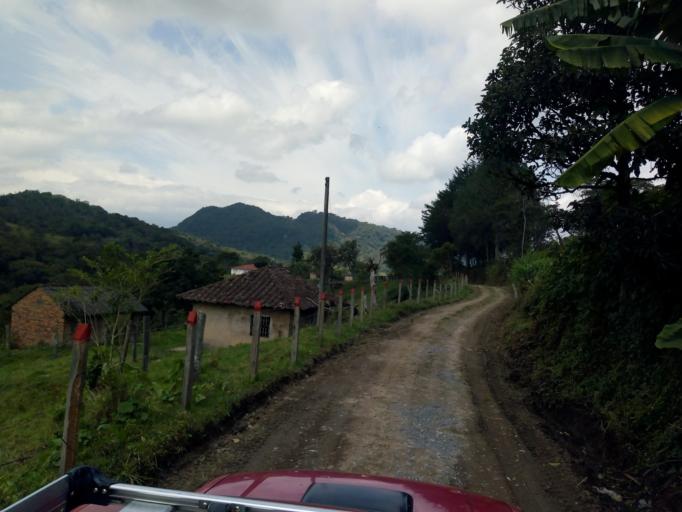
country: CO
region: Boyaca
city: Moniquira
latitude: 5.8657
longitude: -73.5162
